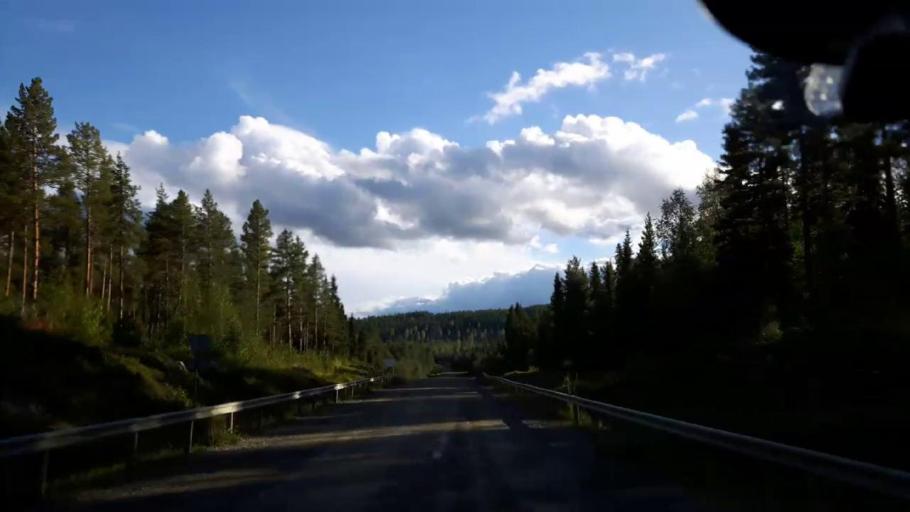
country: SE
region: Jaemtland
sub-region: Stroemsunds Kommun
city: Stroemsund
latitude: 63.3618
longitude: 15.5691
